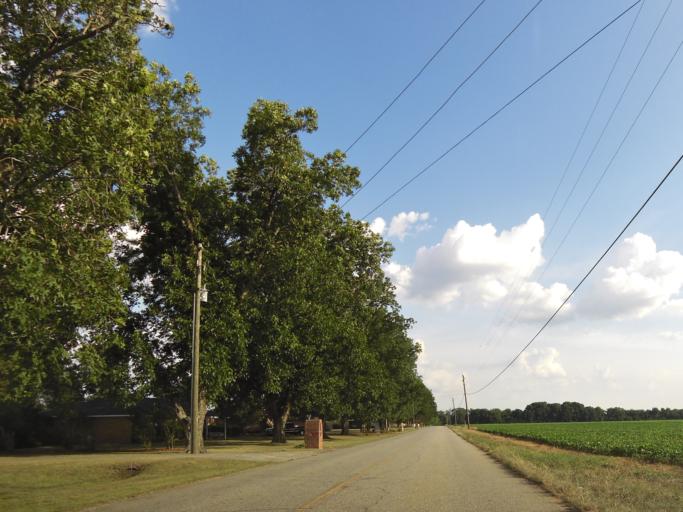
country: US
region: Georgia
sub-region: Houston County
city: Centerville
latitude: 32.7148
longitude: -83.6792
